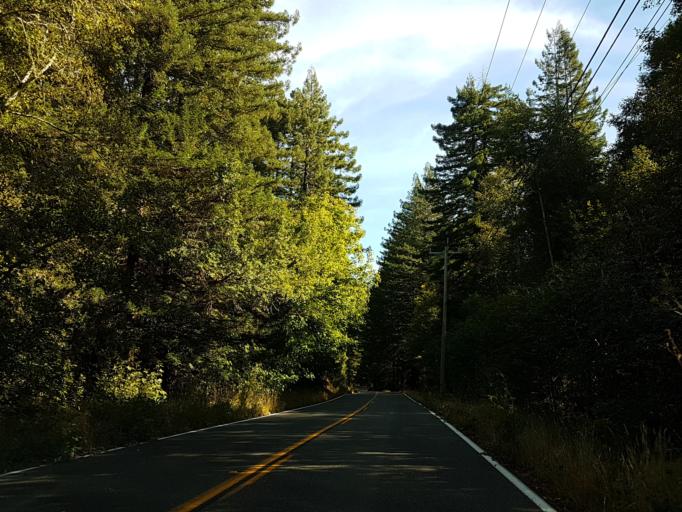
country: US
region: California
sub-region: Humboldt County
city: Rio Dell
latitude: 40.4120
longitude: -123.9587
